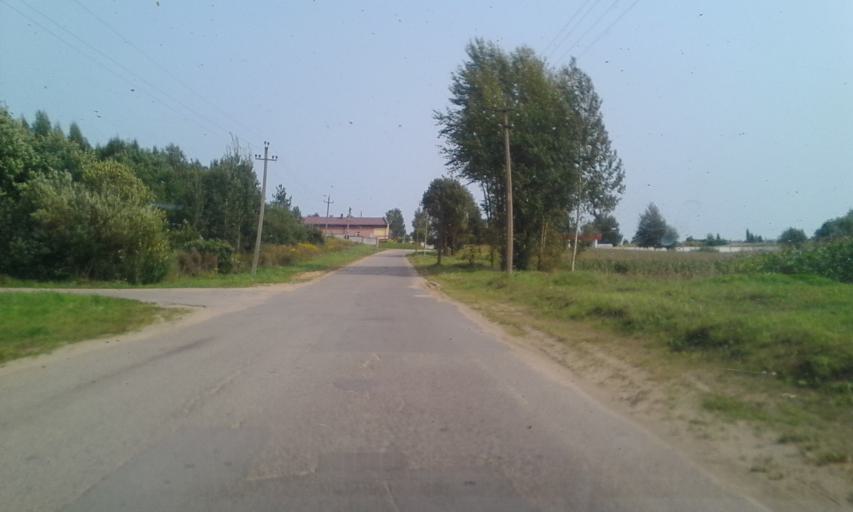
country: BY
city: Michanovichi
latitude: 53.7634
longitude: 27.6923
